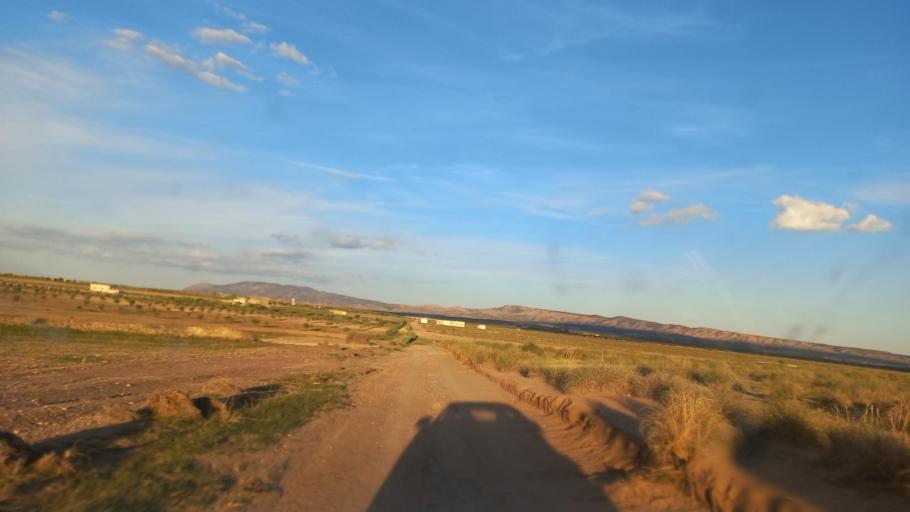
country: TN
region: Al Qasrayn
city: Sbiba
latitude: 35.3483
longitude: 9.0324
